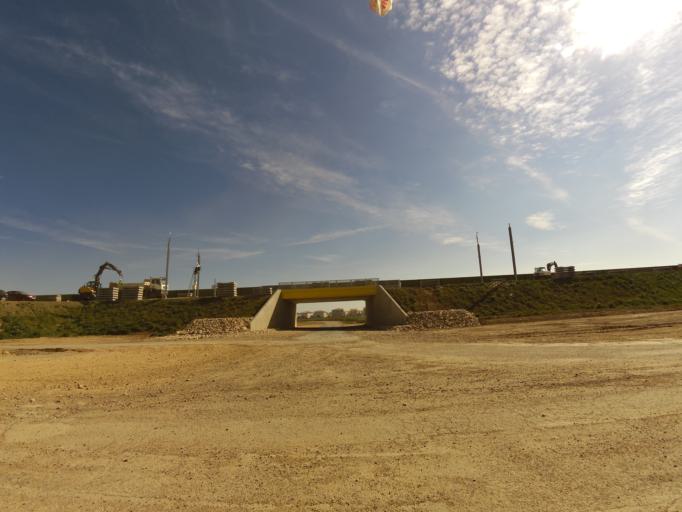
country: FR
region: Languedoc-Roussillon
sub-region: Departement du Gard
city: Aimargues
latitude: 43.7058
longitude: 4.2009
